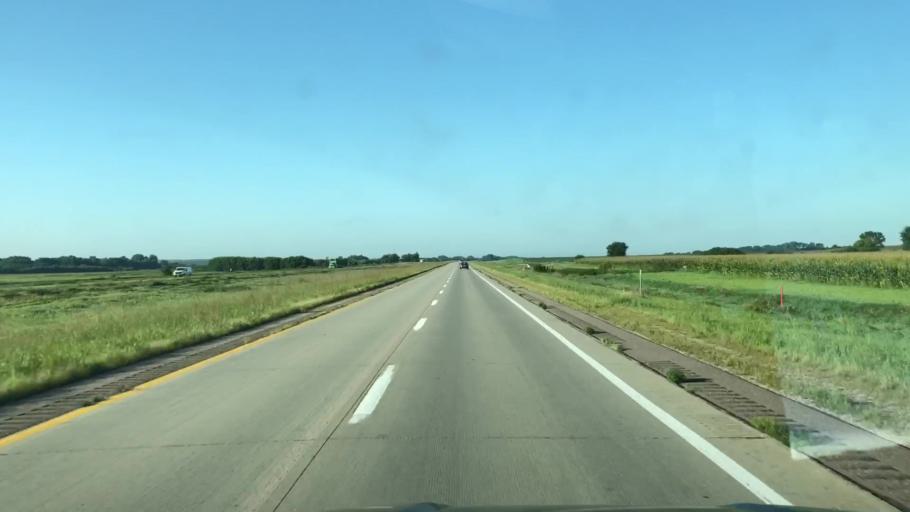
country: US
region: Iowa
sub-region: Sioux County
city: Orange City
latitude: 42.8912
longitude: -96.0929
